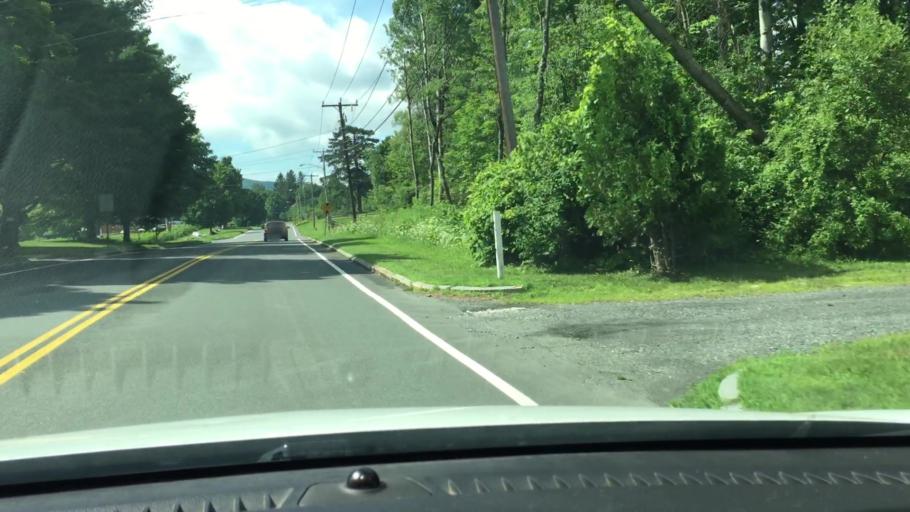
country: US
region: Massachusetts
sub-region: Berkshire County
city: Pittsfield
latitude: 42.4467
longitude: -73.3001
